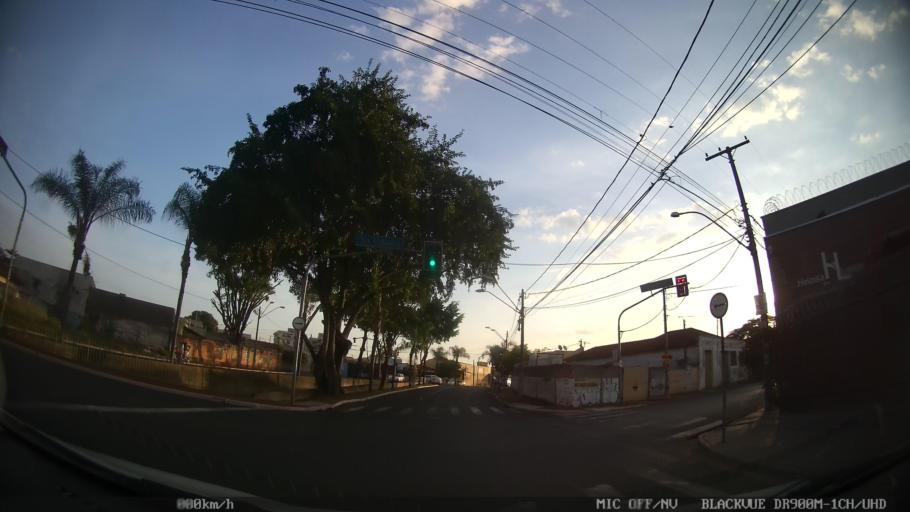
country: BR
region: Sao Paulo
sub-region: Ribeirao Preto
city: Ribeirao Preto
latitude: -21.1644
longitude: -47.8184
